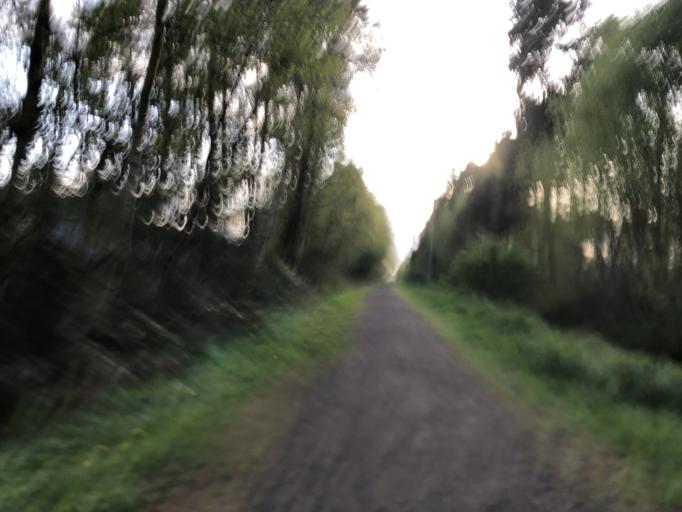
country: CA
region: British Columbia
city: Richmond
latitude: 49.1480
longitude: -123.1059
